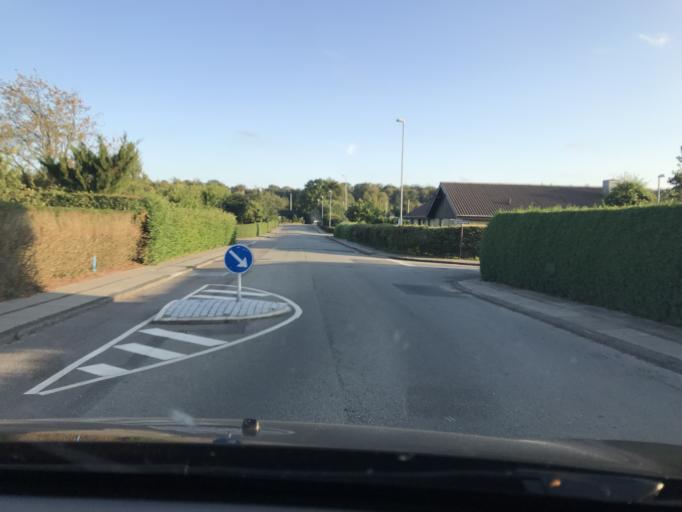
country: DK
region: South Denmark
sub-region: Vejle Kommune
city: Vejle
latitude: 55.7179
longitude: 9.5710
